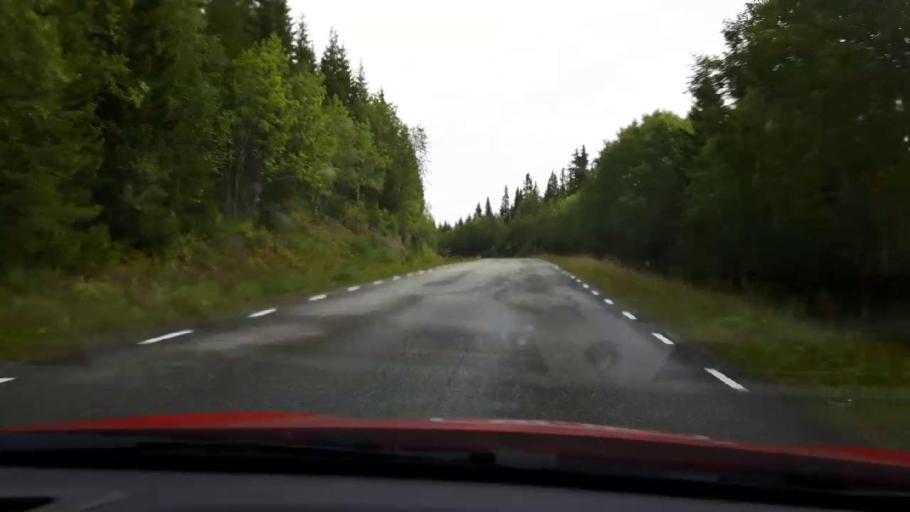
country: SE
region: Jaemtland
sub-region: Are Kommun
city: Are
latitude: 63.7275
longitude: 12.9853
